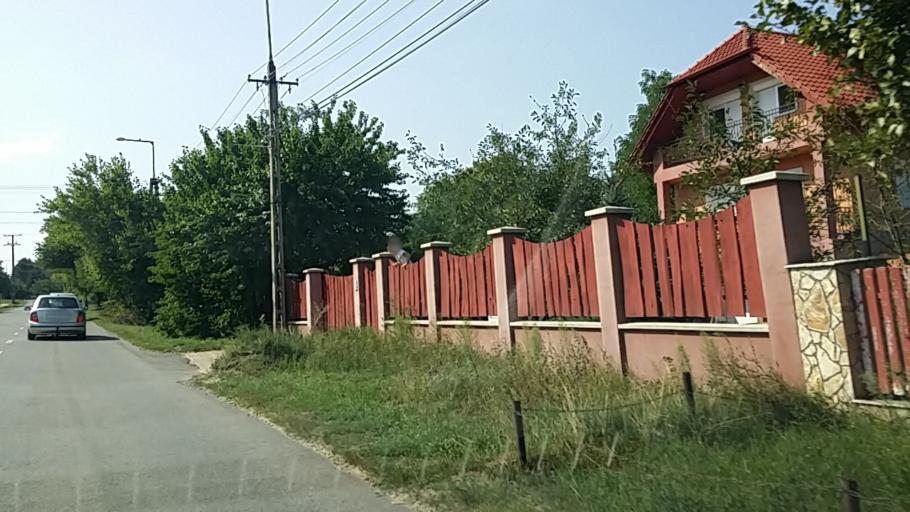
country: HU
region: Pest
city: Erdokertes
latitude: 47.6741
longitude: 19.3187
